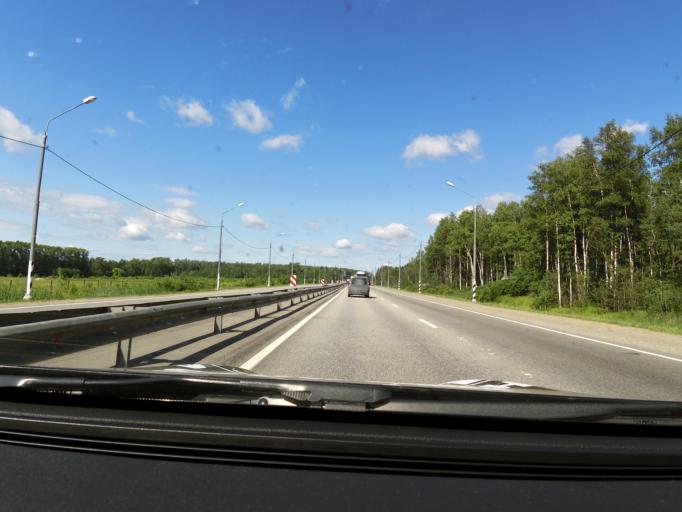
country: RU
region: Tverskaya
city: Likhoslavl'
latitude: 56.9509
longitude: 35.4224
